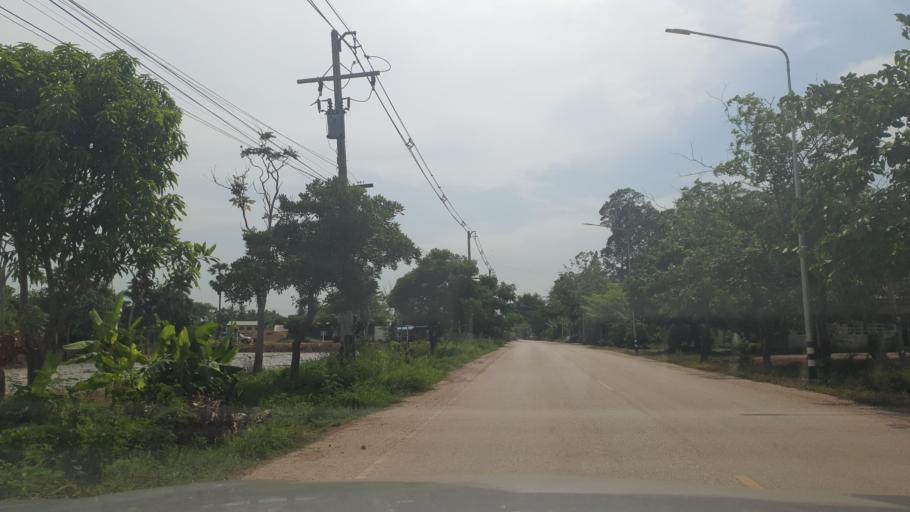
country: TH
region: Sukhothai
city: Si Samrong
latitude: 17.1413
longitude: 99.8327
